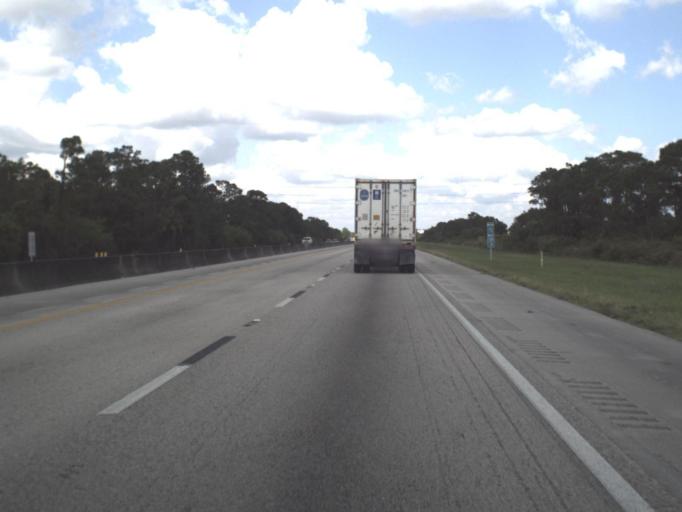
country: US
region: Florida
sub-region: Martin County
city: Port Salerno
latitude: 27.0855
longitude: -80.2528
